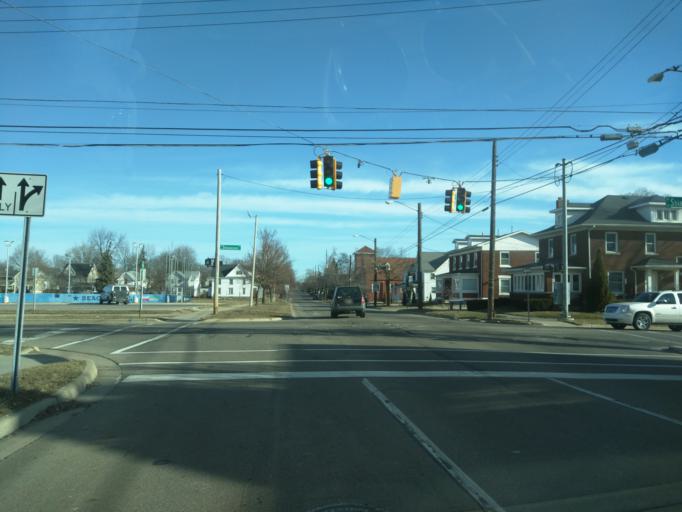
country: US
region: Michigan
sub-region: Ingham County
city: Lansing
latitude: 42.7370
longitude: -84.5570
